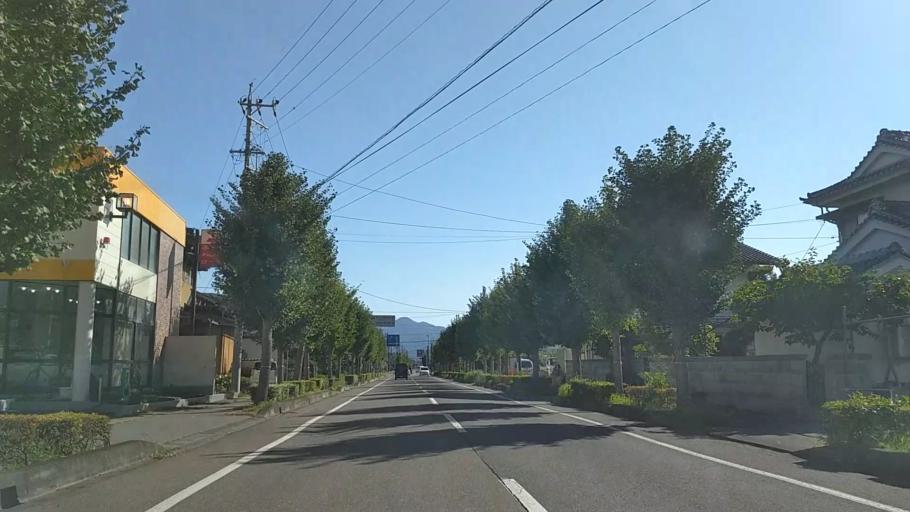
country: JP
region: Nagano
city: Nagano-shi
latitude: 36.5848
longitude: 138.1372
